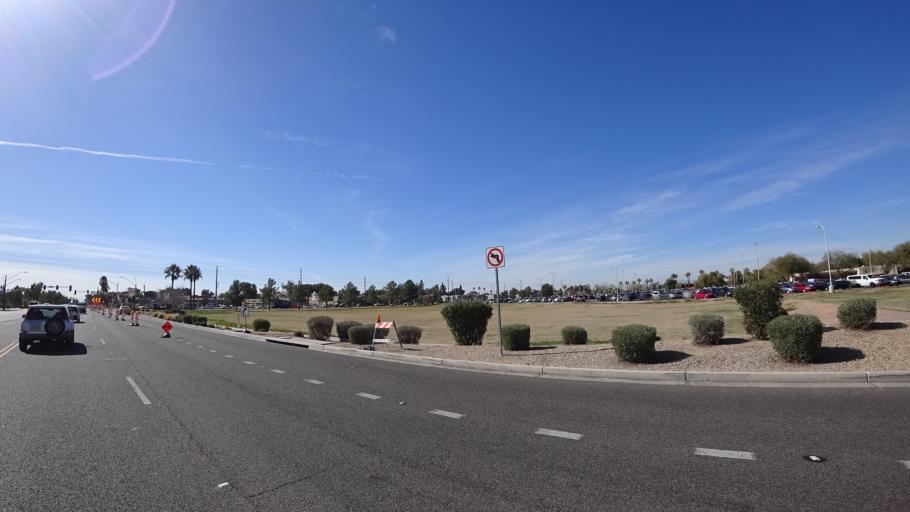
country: US
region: Arizona
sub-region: Maricopa County
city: Glendale
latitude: 33.5689
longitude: -112.1864
